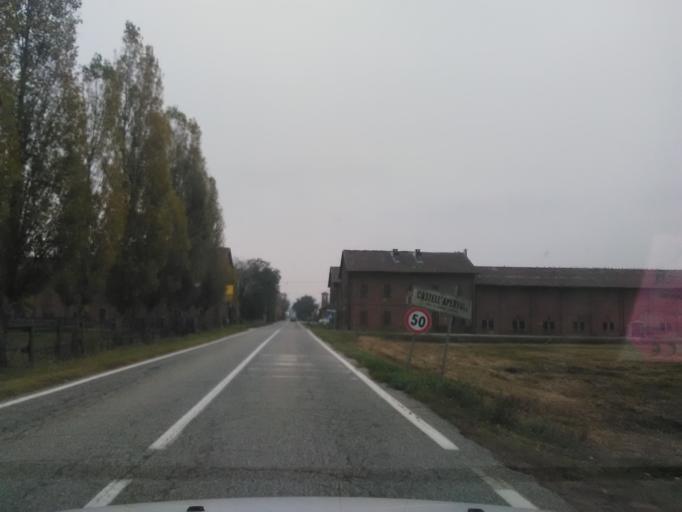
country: IT
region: Piedmont
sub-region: Provincia di Vercelli
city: Fontanetto Po
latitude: 45.2452
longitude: 8.1764
